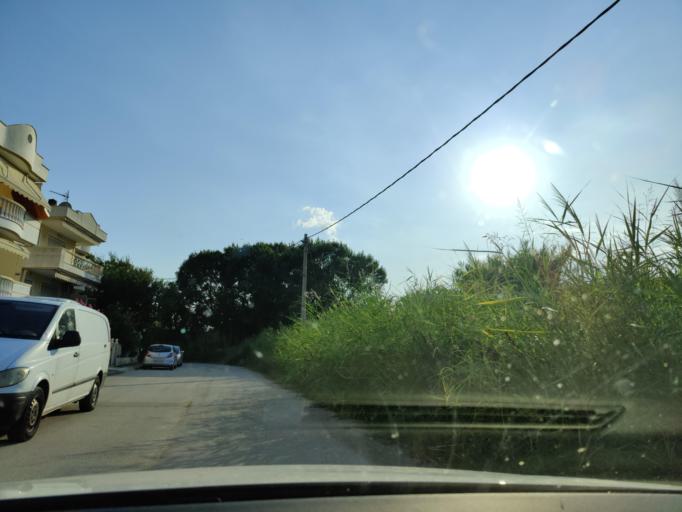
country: GR
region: East Macedonia and Thrace
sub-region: Nomos Kavalas
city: Nea Peramos
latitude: 40.8321
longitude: 24.3032
